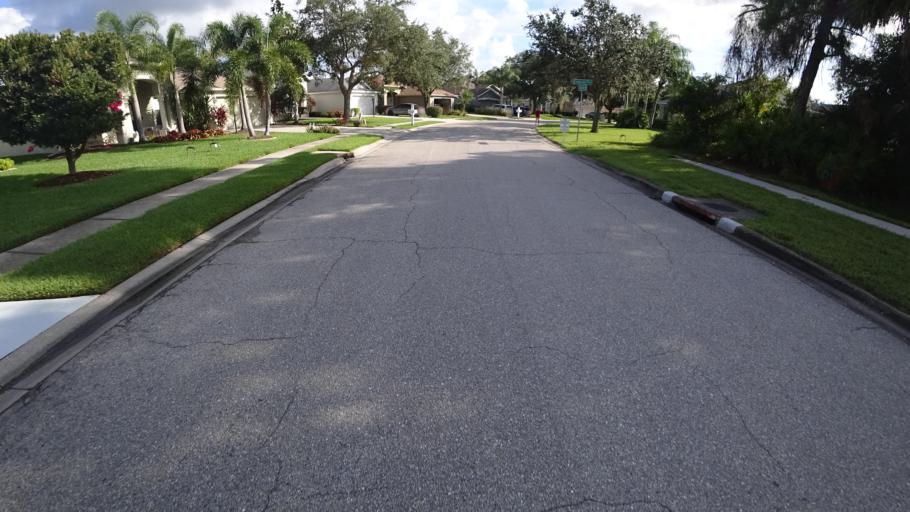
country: US
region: Florida
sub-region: Sarasota County
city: Desoto Lakes
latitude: 27.4215
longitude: -82.4956
